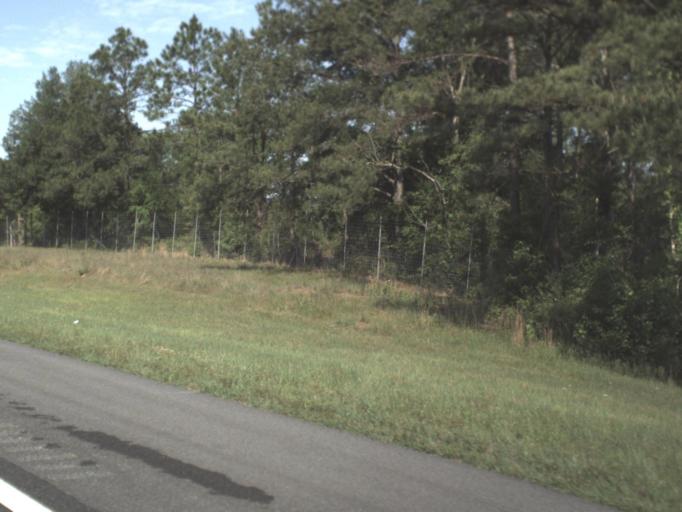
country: US
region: Florida
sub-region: Walton County
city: DeFuniak Springs
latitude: 30.7211
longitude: -85.9184
